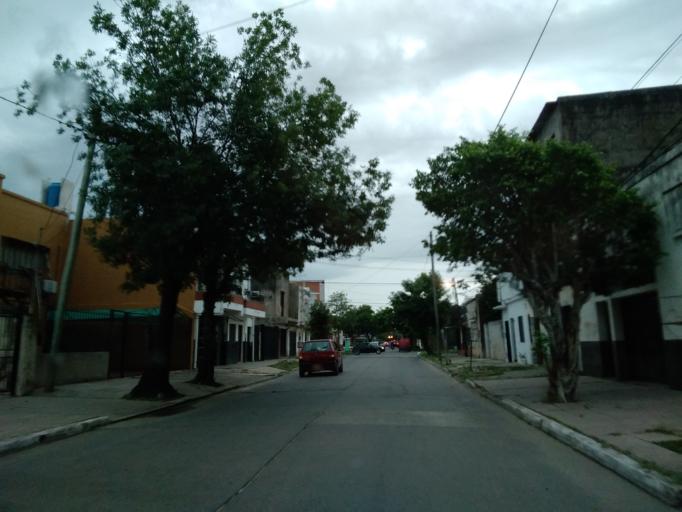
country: AR
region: Corrientes
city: Corrientes
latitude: -27.4788
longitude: -58.8238
